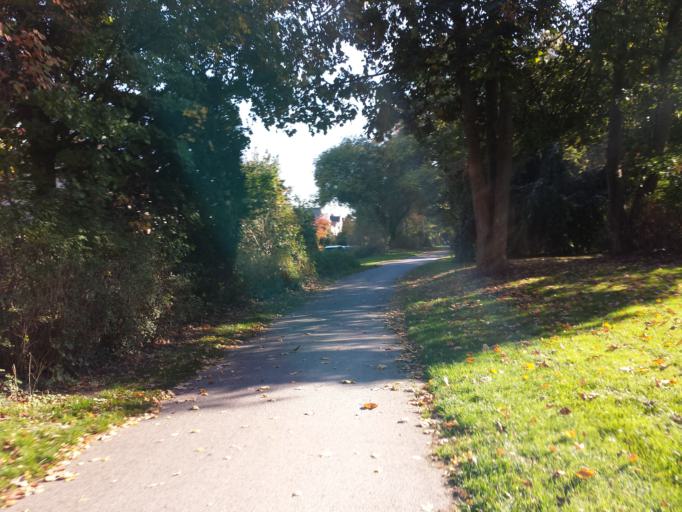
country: DE
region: Lower Saxony
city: Ritterhude
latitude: 53.1328
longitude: 8.7409
